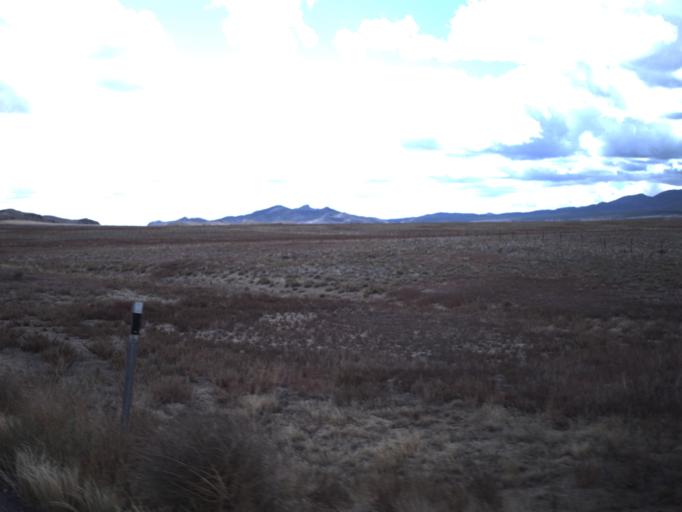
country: US
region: Utah
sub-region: Beaver County
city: Milford
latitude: 38.6374
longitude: -113.8591
